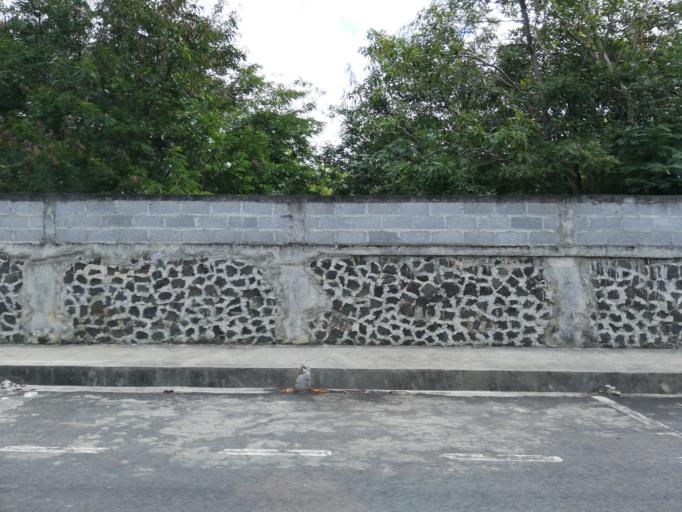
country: MU
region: Port Louis
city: Port Louis
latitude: -20.1630
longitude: 57.4816
